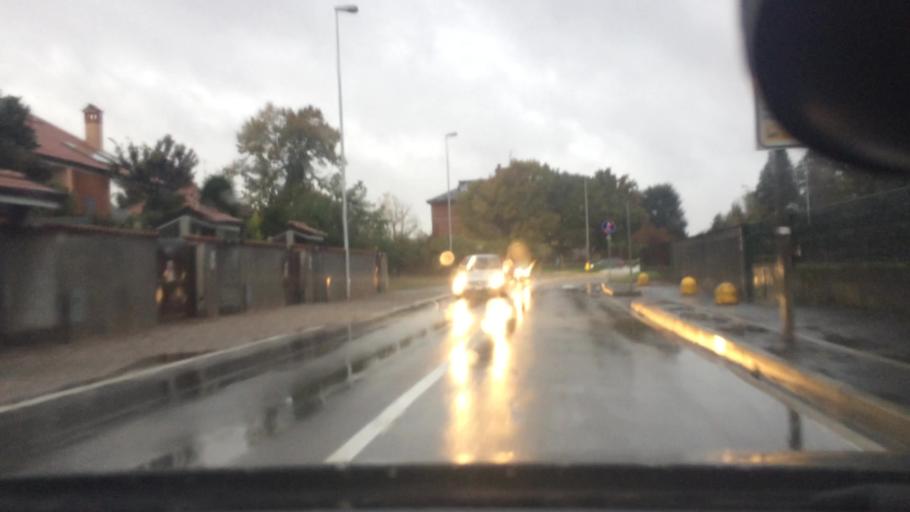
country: IT
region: Lombardy
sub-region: Citta metropolitana di Milano
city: Nerviano
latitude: 45.5472
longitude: 8.9765
